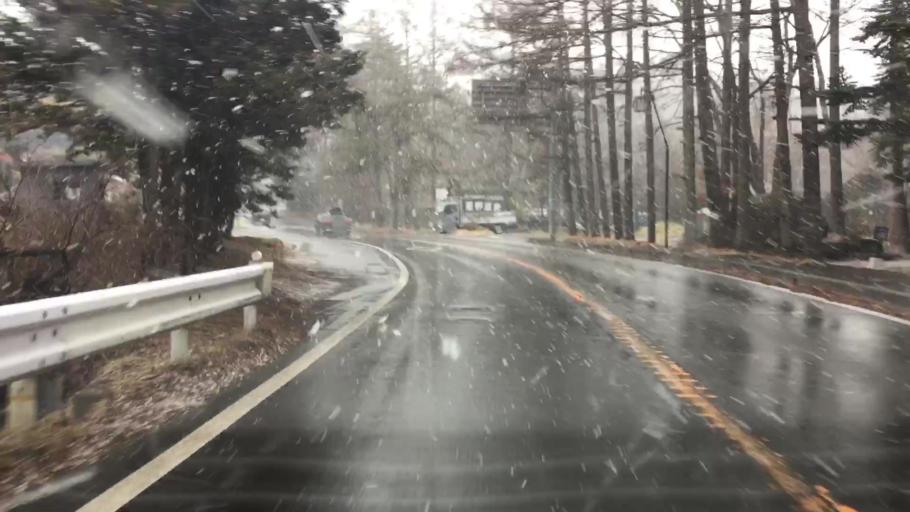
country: JP
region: Nagano
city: Komoro
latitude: 36.3608
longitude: 138.5889
